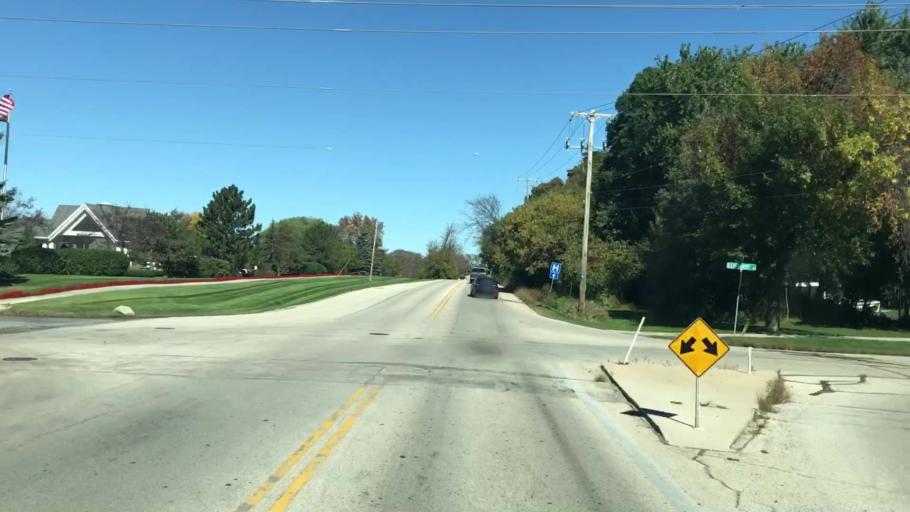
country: US
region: Wisconsin
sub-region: Waukesha County
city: Brookfield
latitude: 43.0539
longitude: -88.1664
